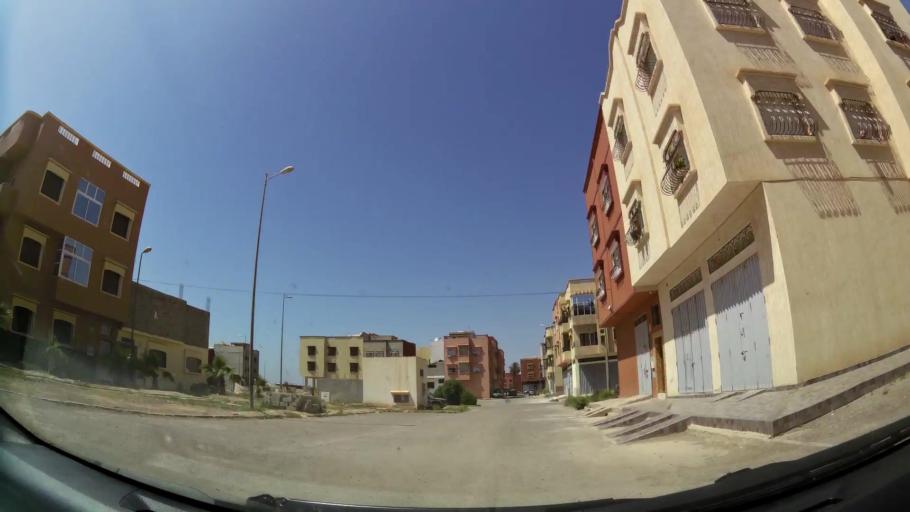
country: MA
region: Souss-Massa-Draa
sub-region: Inezgane-Ait Mellou
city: Inezgane
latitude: 30.3442
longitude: -9.5191
